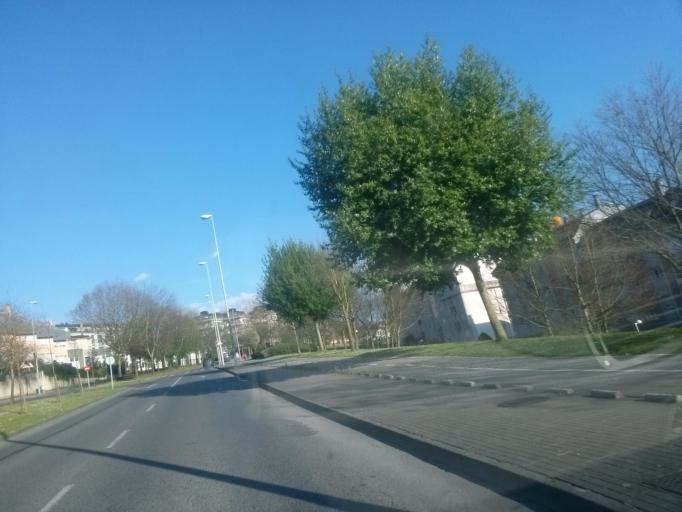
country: ES
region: Galicia
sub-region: Provincia de Lugo
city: Lugo
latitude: 43.0025
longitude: -7.5570
